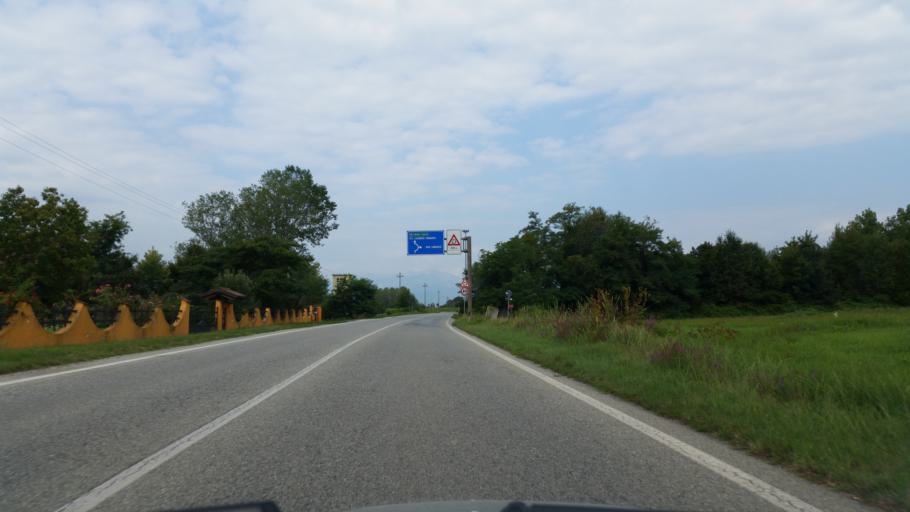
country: IT
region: Piedmont
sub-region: Provincia di Torino
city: Orio Canavese
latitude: 45.3095
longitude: 7.8514
